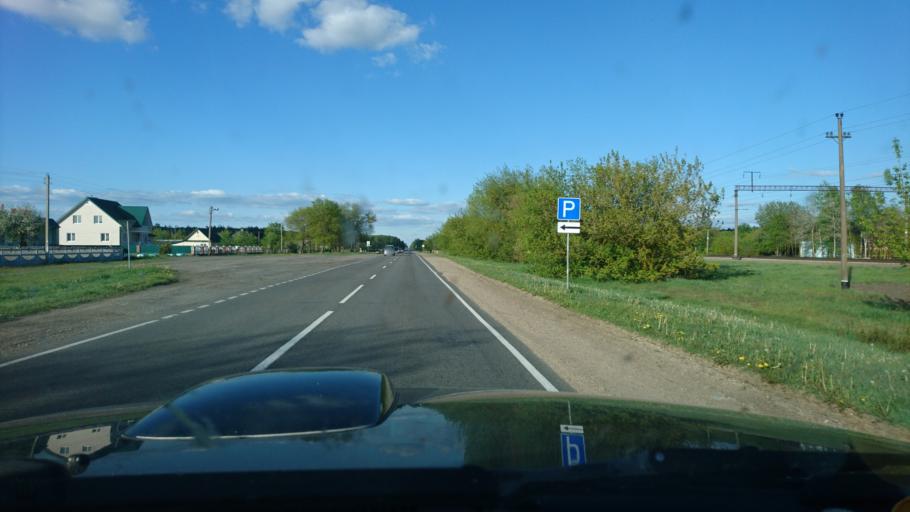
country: BY
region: Brest
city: Nyakhachava
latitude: 52.6491
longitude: 25.2160
